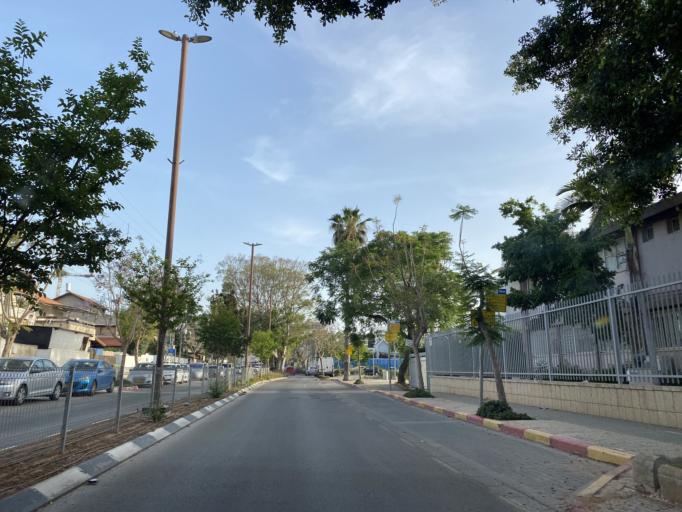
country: IL
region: Tel Aviv
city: Herzliyya
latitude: 32.1651
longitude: 34.8305
